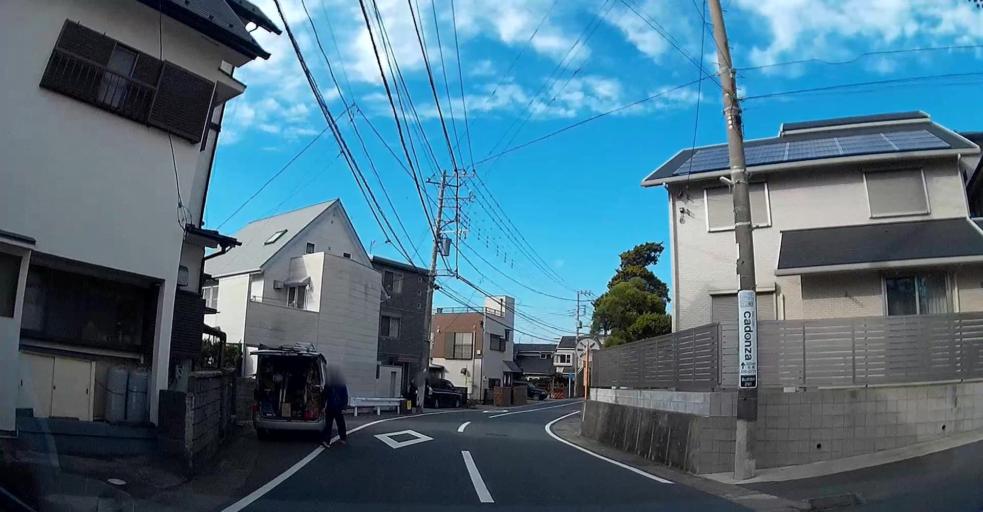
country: JP
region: Kanagawa
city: Hayama
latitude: 35.2790
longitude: 139.5713
